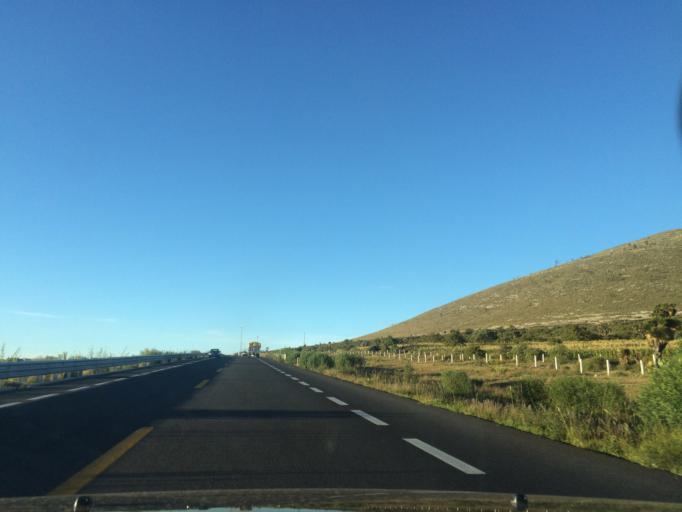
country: MX
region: Puebla
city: Morelos Canada
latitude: 18.7263
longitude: -97.4739
